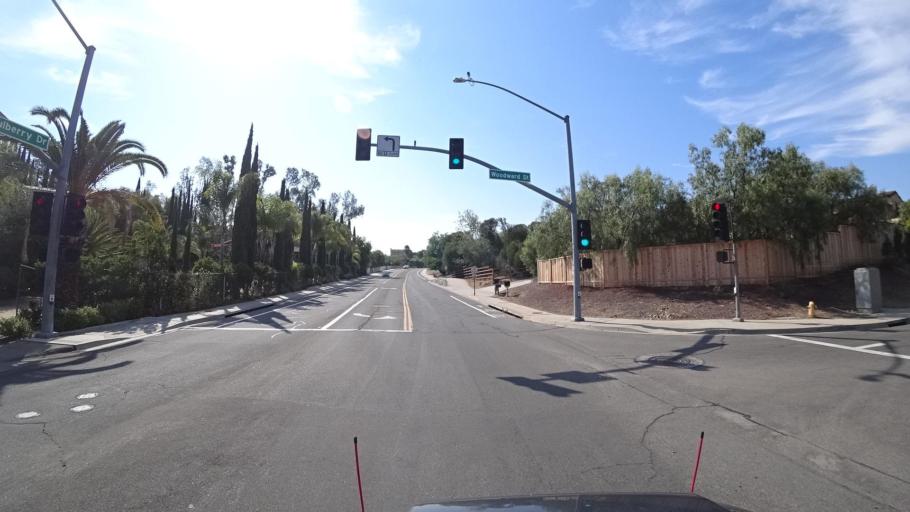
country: US
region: California
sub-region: San Diego County
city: San Marcos
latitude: 33.1662
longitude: -117.1517
